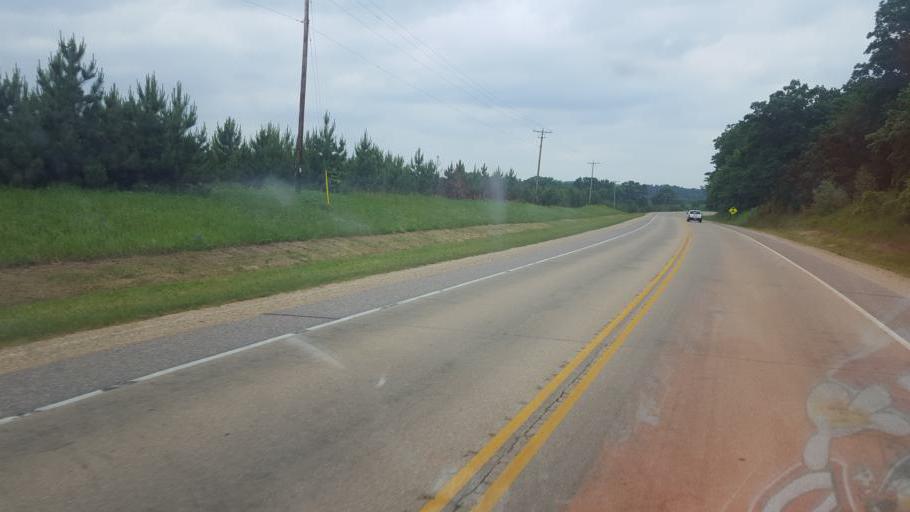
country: US
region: Wisconsin
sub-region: Juneau County
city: Elroy
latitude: 43.6350
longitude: -90.1769
